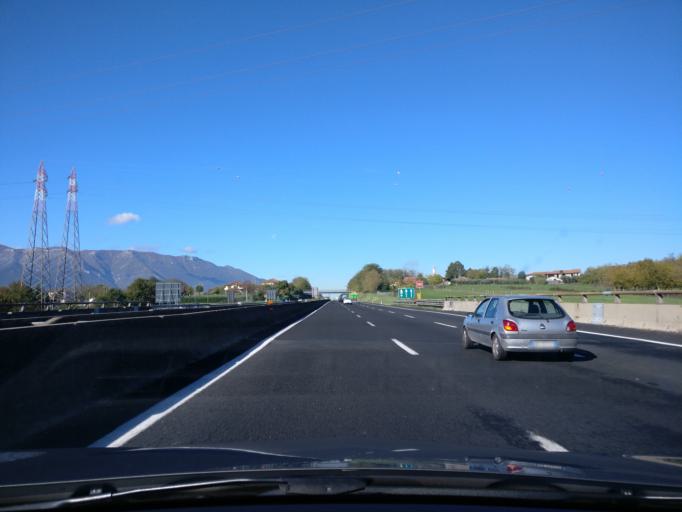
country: IT
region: Latium
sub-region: Provincia di Frosinone
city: Frosinone
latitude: 41.6217
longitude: 13.3066
